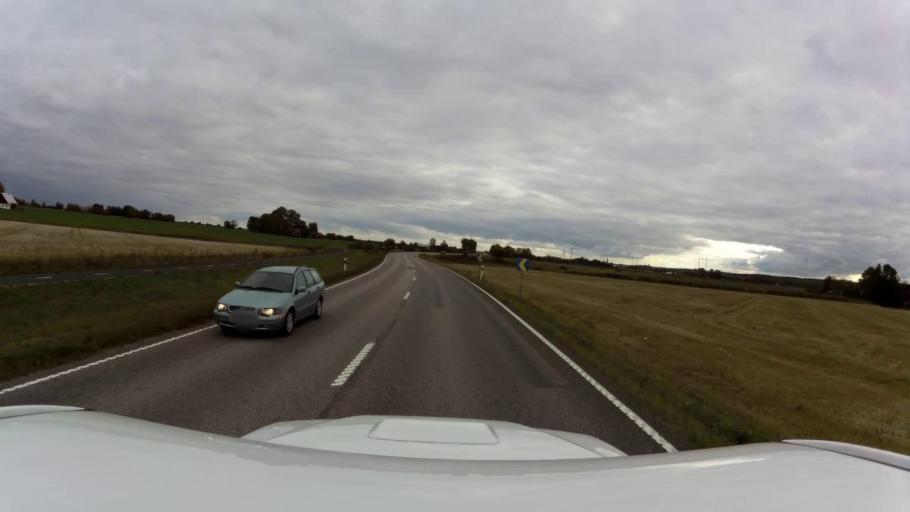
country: SE
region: OEstergoetland
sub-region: Linkopings Kommun
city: Berg
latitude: 58.4456
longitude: 15.5669
